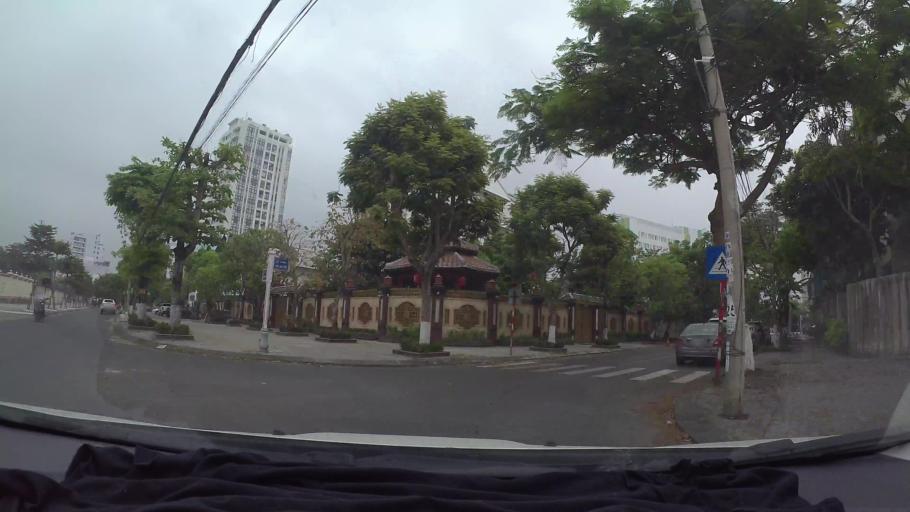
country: VN
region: Da Nang
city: Cam Le
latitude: 16.0386
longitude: 108.2095
